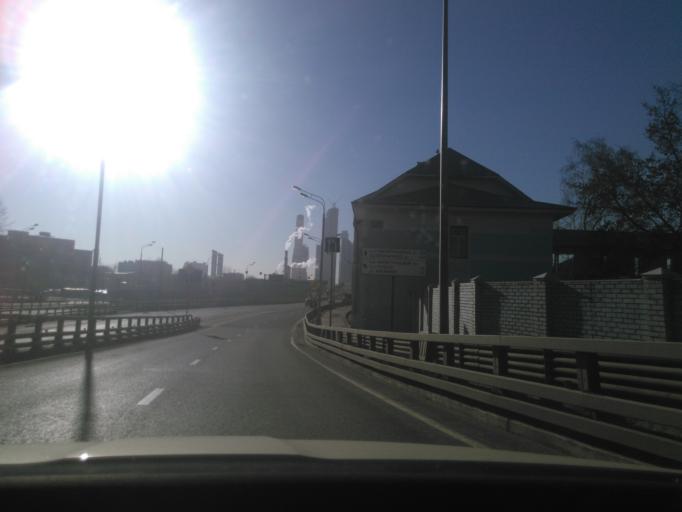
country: RU
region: Moscow
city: Sokol
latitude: 55.7671
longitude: 37.5174
